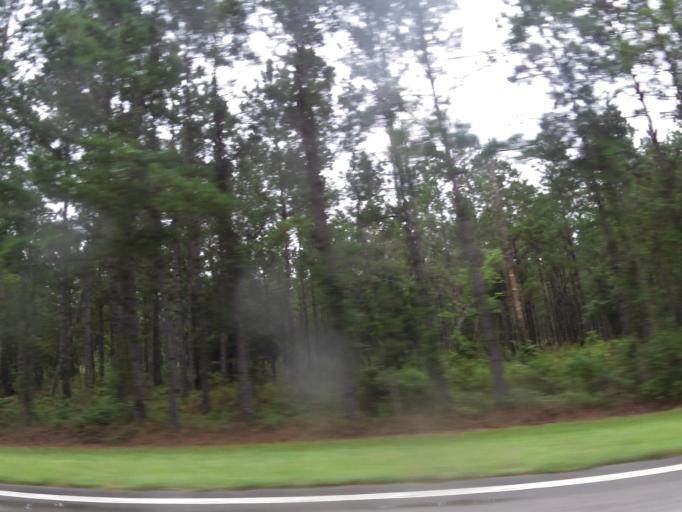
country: US
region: Florida
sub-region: Saint Johns County
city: Saint Augustine South
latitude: 29.8555
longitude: -81.4586
